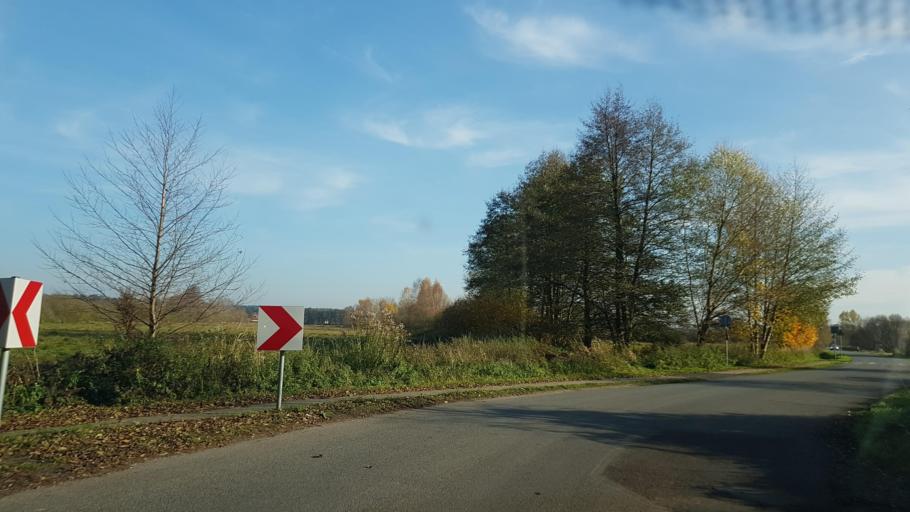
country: PL
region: West Pomeranian Voivodeship
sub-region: Powiat policki
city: Dobra
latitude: 53.4967
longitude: 14.3633
